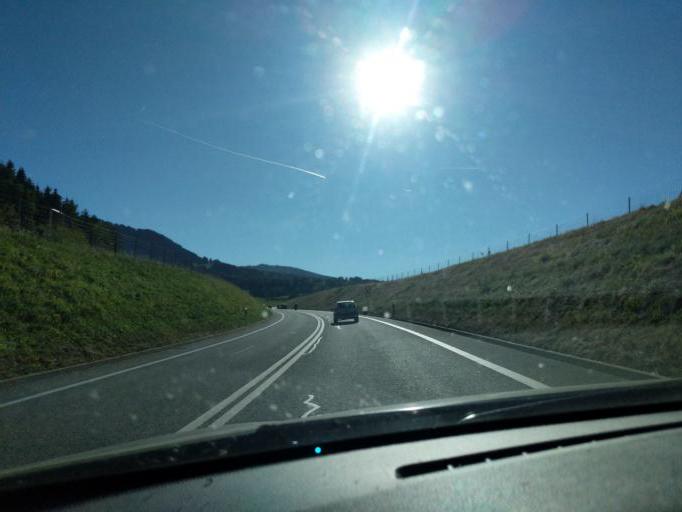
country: CH
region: Fribourg
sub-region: Gruyere District
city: La Tour-de-Treme
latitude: 46.6044
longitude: 7.0680
